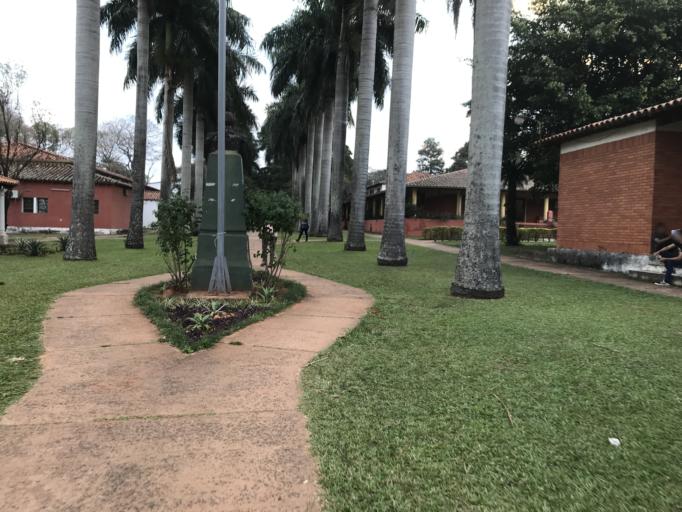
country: PY
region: Central
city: San Lorenzo
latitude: -25.3359
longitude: -57.5147
